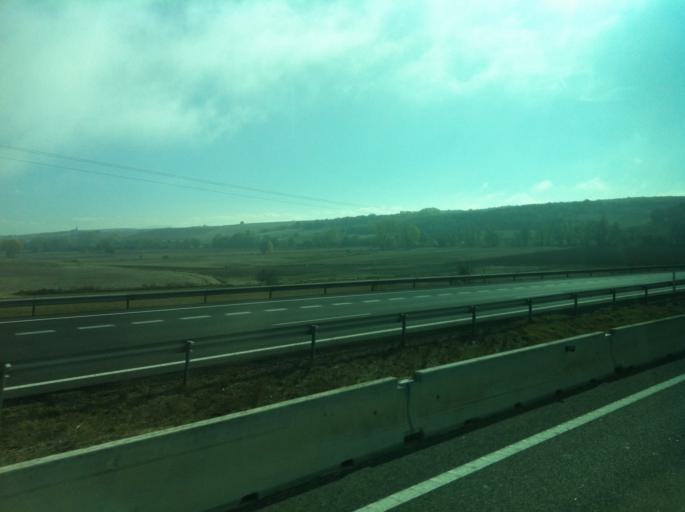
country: ES
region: Castille and Leon
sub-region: Provincia de Burgos
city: Madrigalejo del Monte
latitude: 42.1098
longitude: -3.7183
